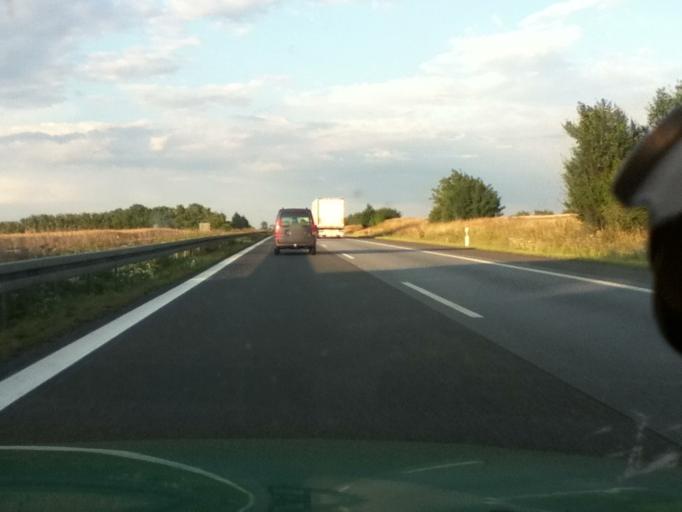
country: DE
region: Saxony
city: Crostwitz
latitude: 51.2018
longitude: 14.2446
